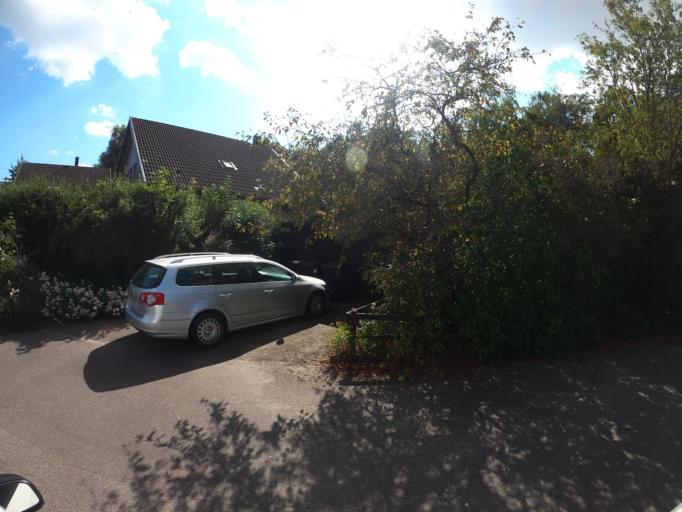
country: SE
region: Skane
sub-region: Lunds Kommun
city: Genarp
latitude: 55.7088
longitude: 13.3380
